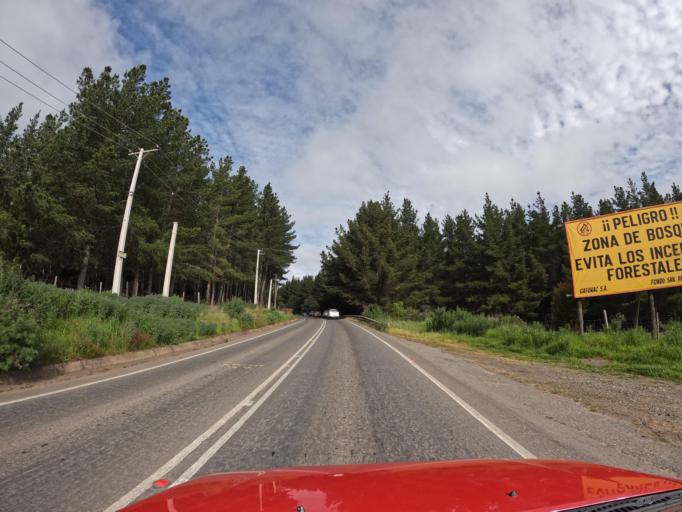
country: CL
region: O'Higgins
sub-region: Provincia de Colchagua
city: Santa Cruz
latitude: -34.3518
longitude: -71.9283
